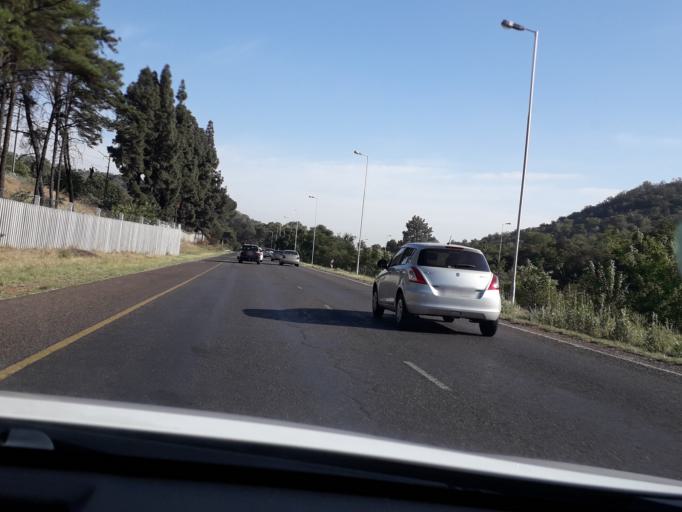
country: ZA
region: Gauteng
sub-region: City of Tshwane Metropolitan Municipality
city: Pretoria
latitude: -25.8002
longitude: 28.1969
